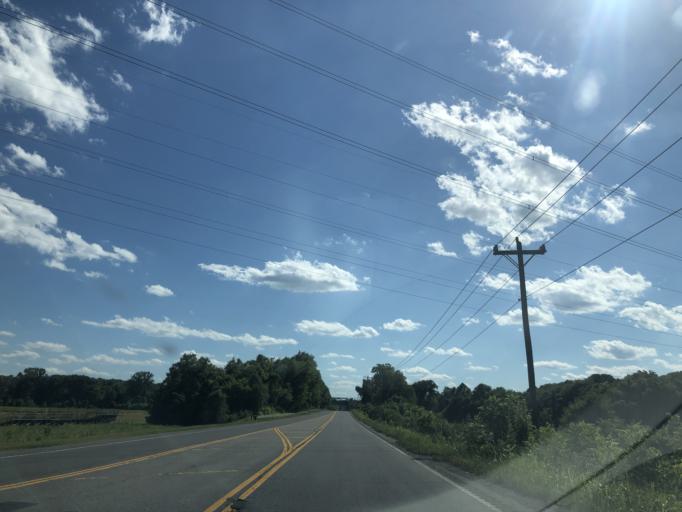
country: US
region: Tennessee
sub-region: Davidson County
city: Belle Meade
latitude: 36.0566
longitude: -86.9249
